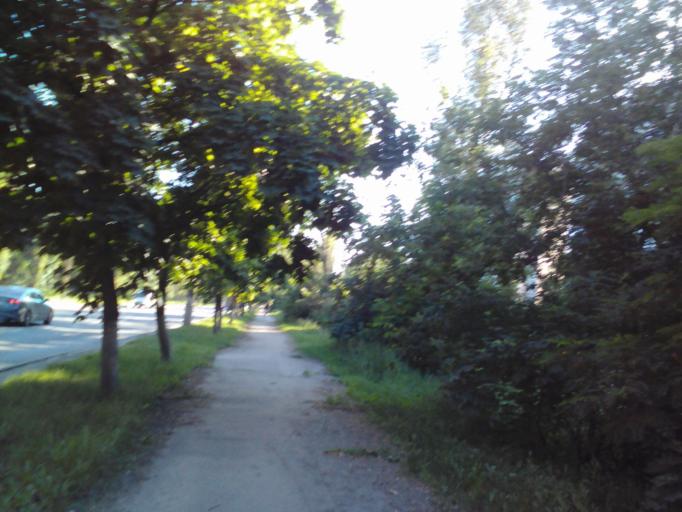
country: RU
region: Kursk
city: Voroshnevo
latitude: 51.6656
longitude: 36.0707
